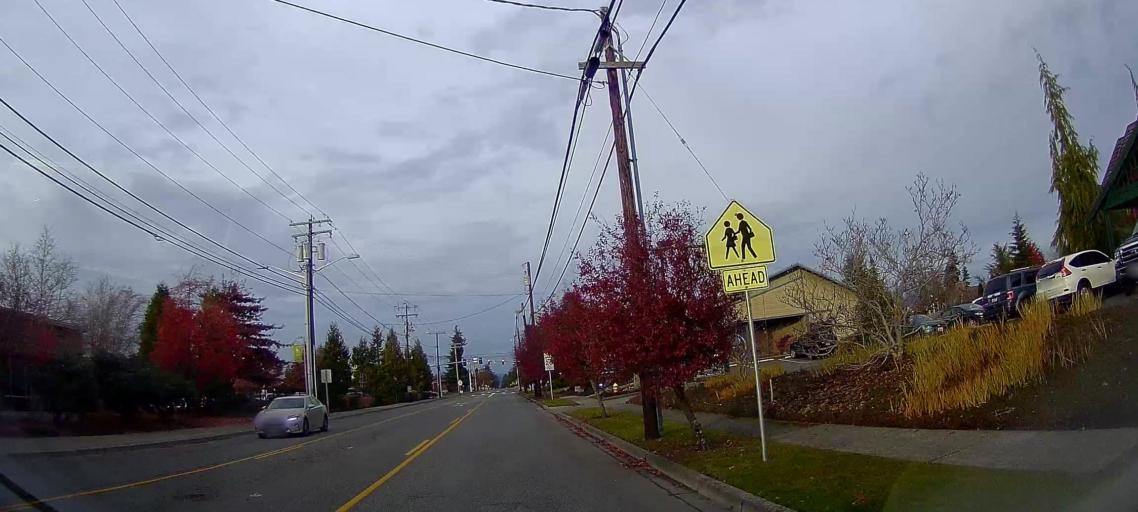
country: US
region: Washington
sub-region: Skagit County
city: Mount Vernon
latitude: 48.4198
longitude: -122.3229
